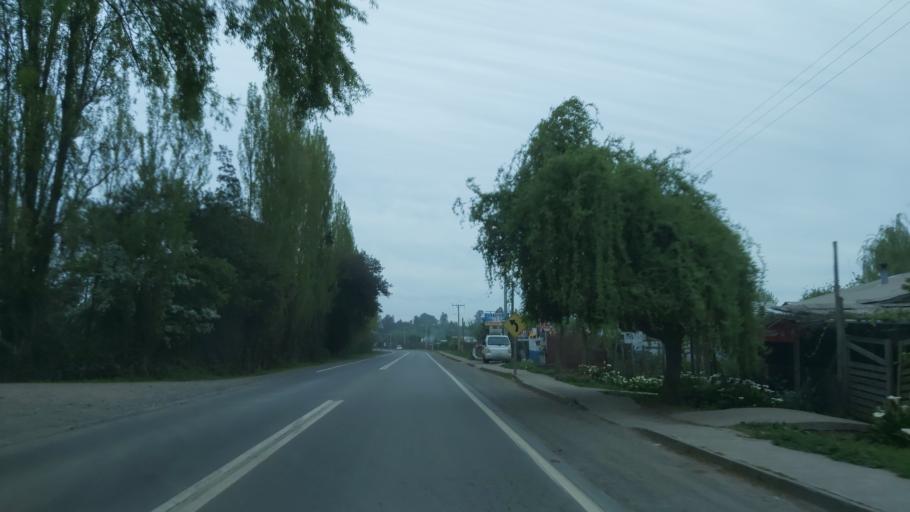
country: CL
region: Maule
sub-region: Provincia de Linares
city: Colbun
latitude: -35.7556
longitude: -71.5000
